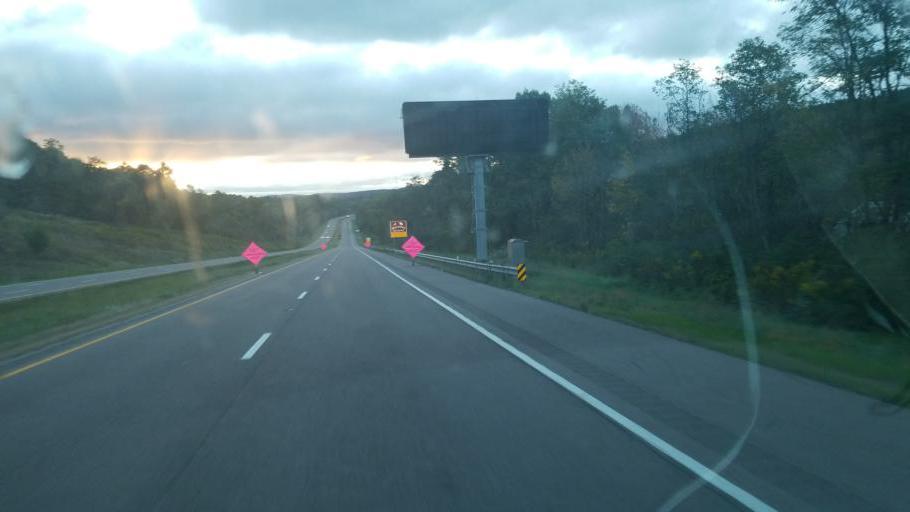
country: US
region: West Virginia
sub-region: Preston County
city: Terra Alta
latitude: 39.6601
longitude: -79.4613
